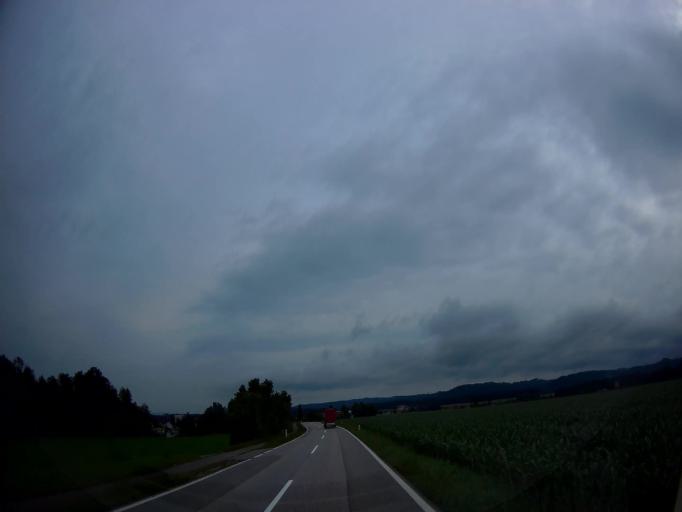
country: AT
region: Salzburg
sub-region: Politischer Bezirk Salzburg-Umgebung
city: Mattsee
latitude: 48.0440
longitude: 13.1489
